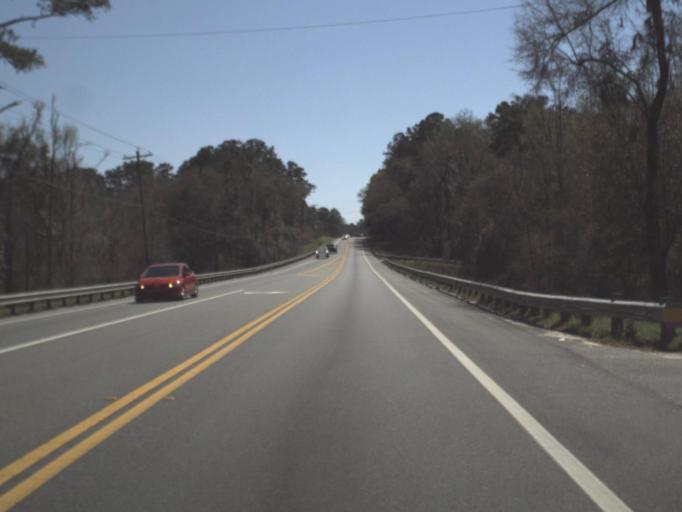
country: US
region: Florida
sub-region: Gadsden County
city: Midway
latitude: 30.4990
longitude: -84.3616
